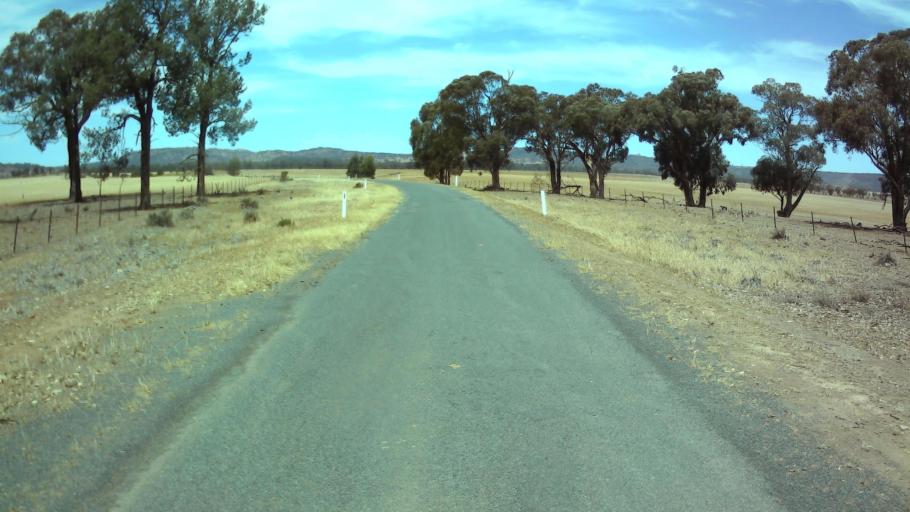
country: AU
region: New South Wales
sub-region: Weddin
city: Grenfell
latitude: -33.7583
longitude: 148.1006
